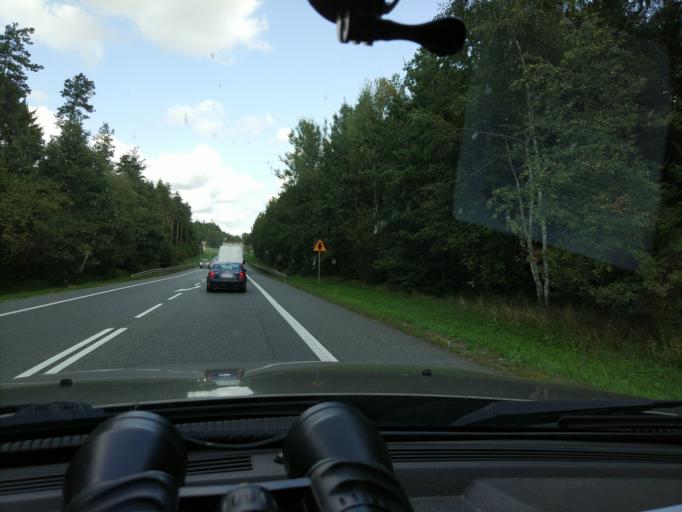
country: PL
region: Masovian Voivodeship
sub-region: Powiat mlawski
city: Mlawa
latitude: 53.1422
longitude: 20.3993
